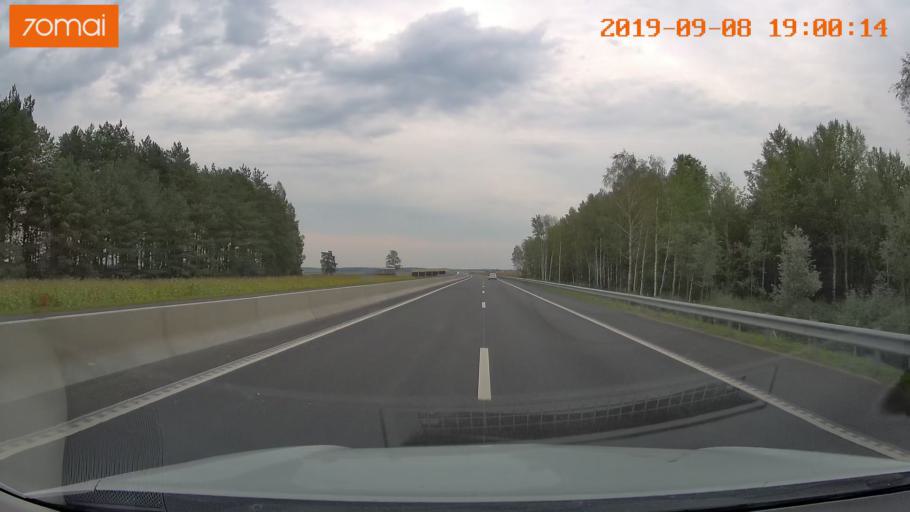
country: BY
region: Grodnenskaya
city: Lyubcha
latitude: 53.9065
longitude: 26.0137
